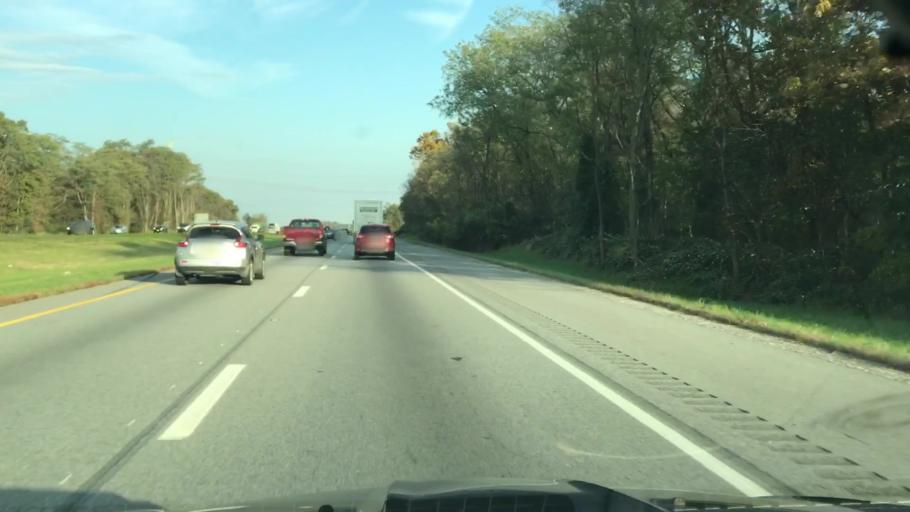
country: US
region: Pennsylvania
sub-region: Cumberland County
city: Schlusser
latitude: 40.2426
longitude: -77.1088
